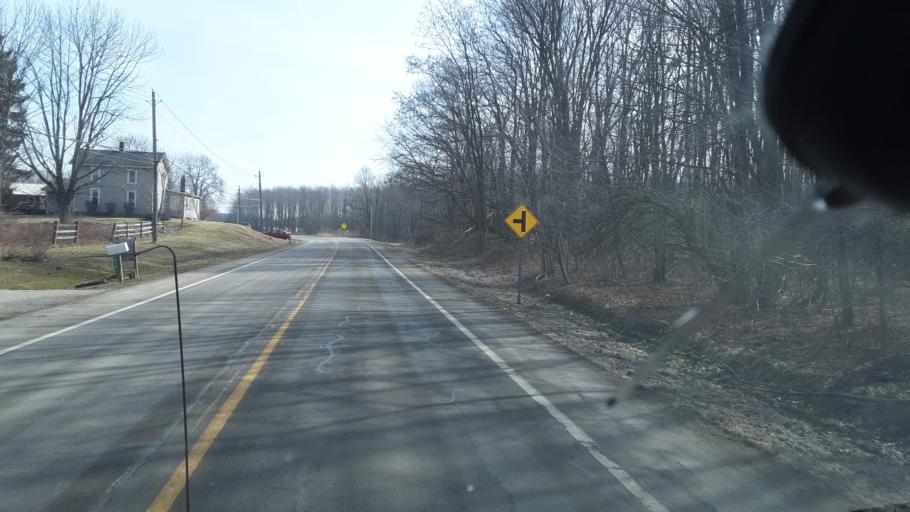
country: US
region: Ohio
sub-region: Ashtabula County
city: Jefferson
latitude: 41.7464
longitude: -80.7438
